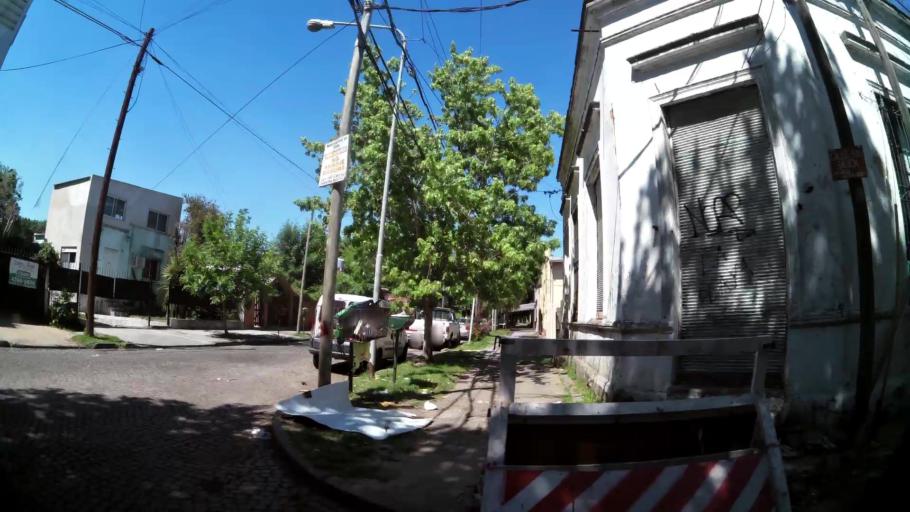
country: AR
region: Buenos Aires
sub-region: Partido de Tigre
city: Tigre
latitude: -34.4316
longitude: -58.5665
